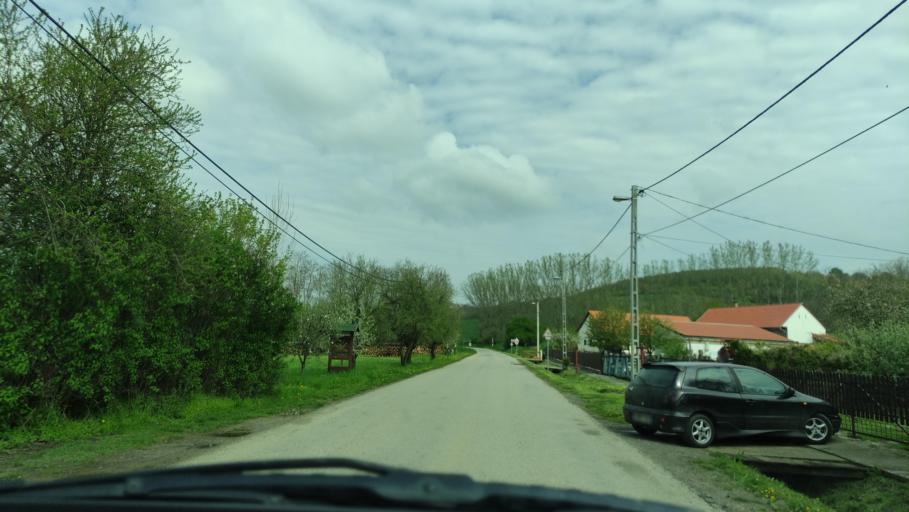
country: HU
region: Baranya
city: Magocs
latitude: 46.2804
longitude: 18.2057
